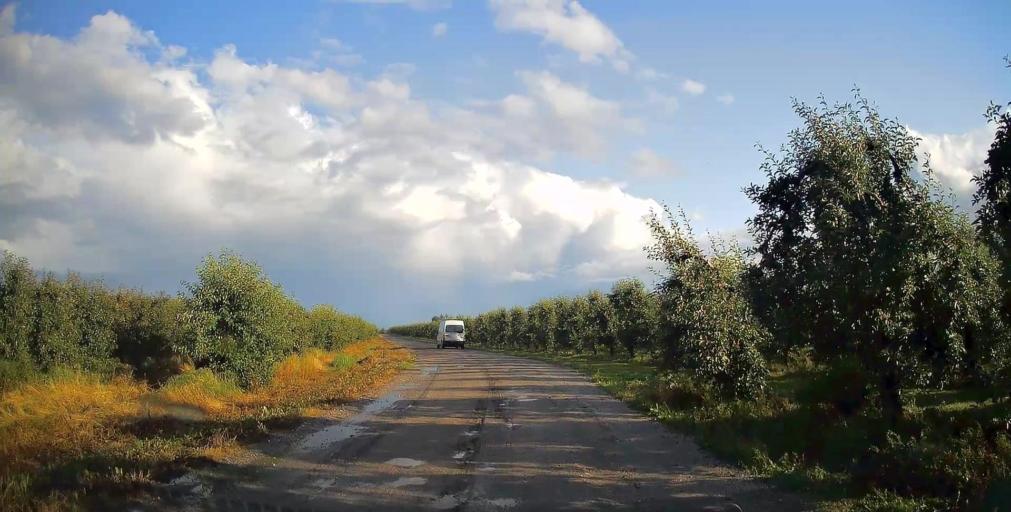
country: PL
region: Masovian Voivodeship
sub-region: Powiat grojecki
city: Goszczyn
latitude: 51.7487
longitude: 20.8860
